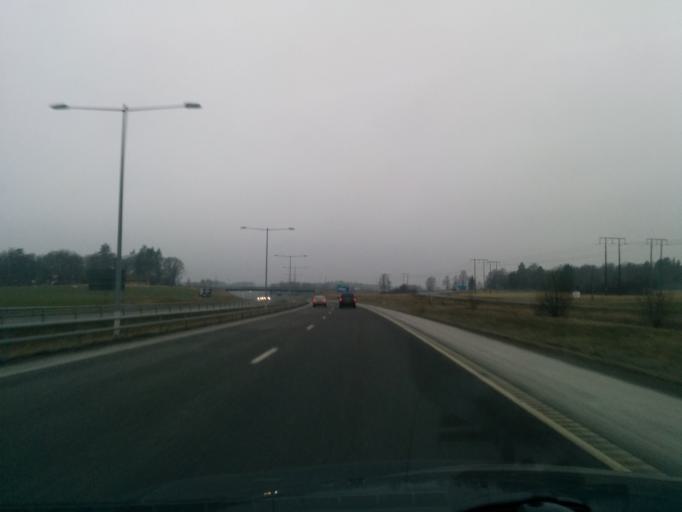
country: SE
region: Stockholm
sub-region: Taby Kommun
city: Taby
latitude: 59.4756
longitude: 18.0273
